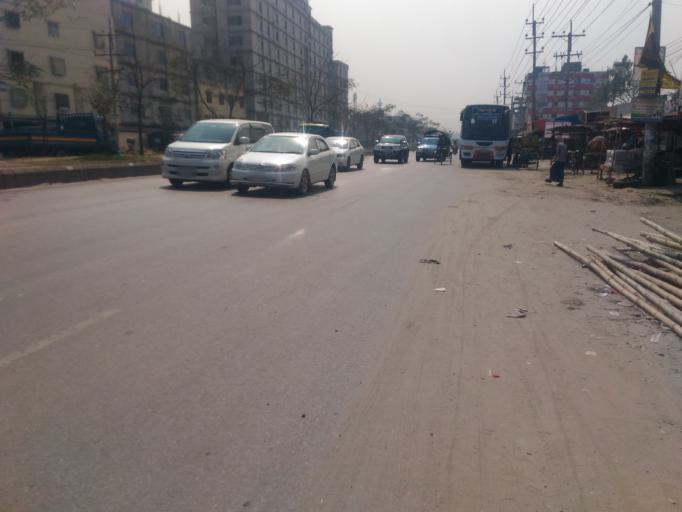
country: BD
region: Dhaka
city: Tungi
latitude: 24.0018
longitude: 90.3828
